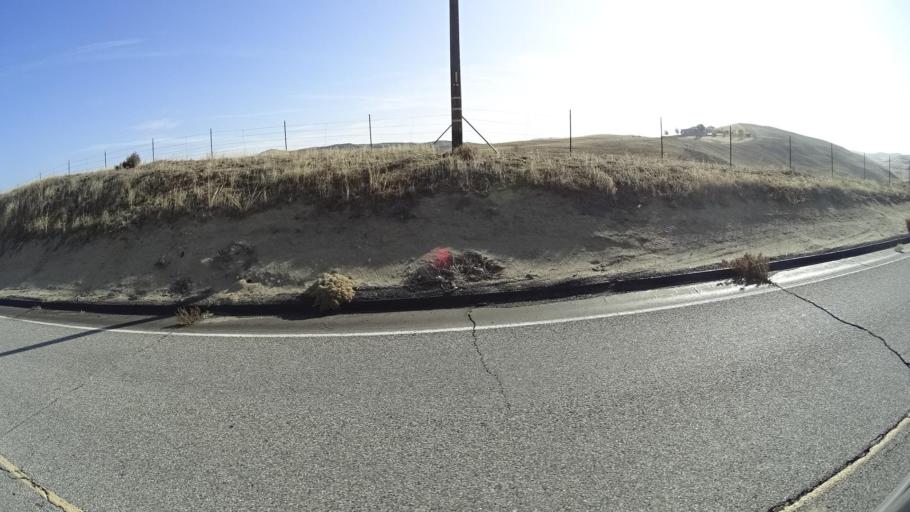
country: US
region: California
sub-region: Kern County
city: Oildale
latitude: 35.5233
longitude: -118.9781
